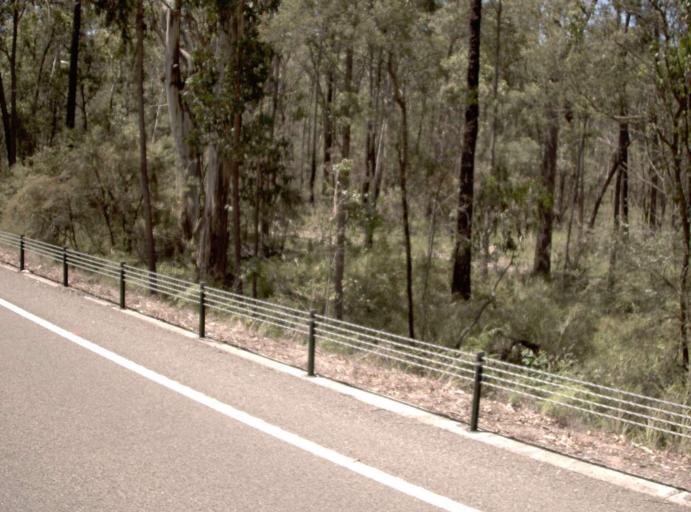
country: AU
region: Victoria
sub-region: East Gippsland
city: Lakes Entrance
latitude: -37.7716
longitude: 148.0562
